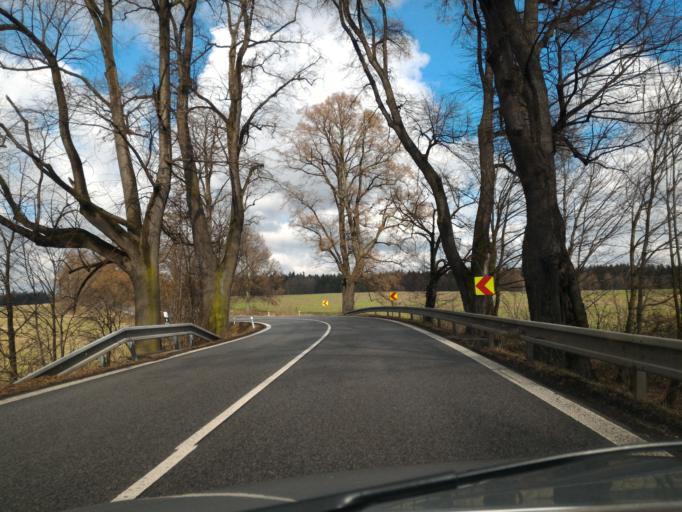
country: PL
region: Silesian Voivodeship
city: Zawidow
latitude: 50.9894
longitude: 15.0777
